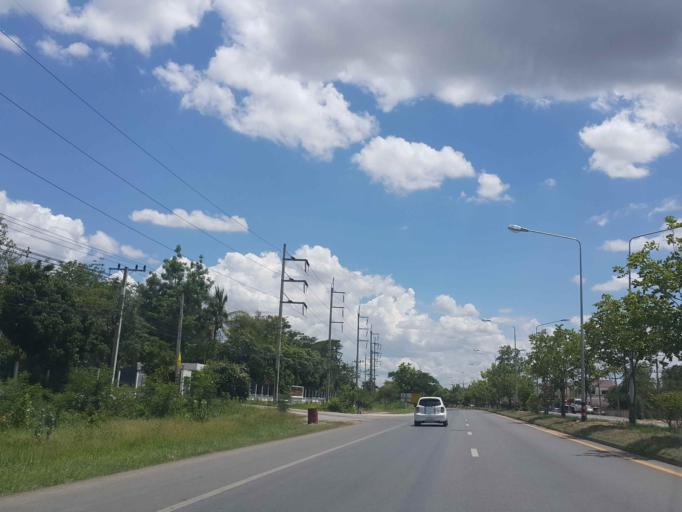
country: TH
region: Phrae
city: Nong Muang Khai
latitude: 18.2351
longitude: 100.2140
